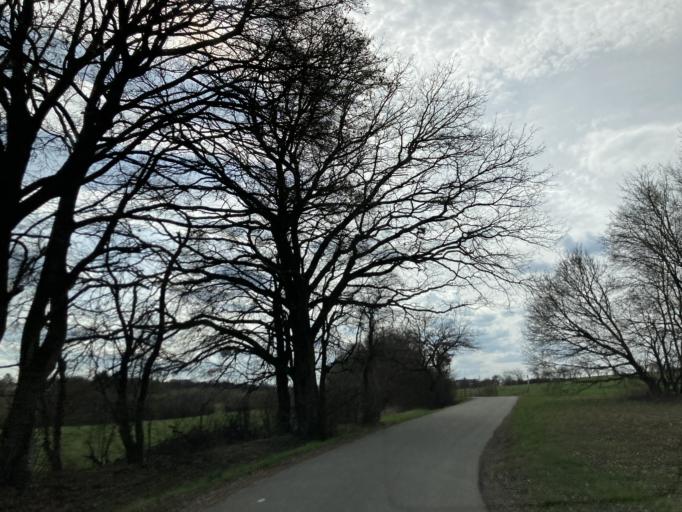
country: DE
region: Baden-Wuerttemberg
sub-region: Tuebingen Region
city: Gomaringen
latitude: 48.4675
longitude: 9.1113
